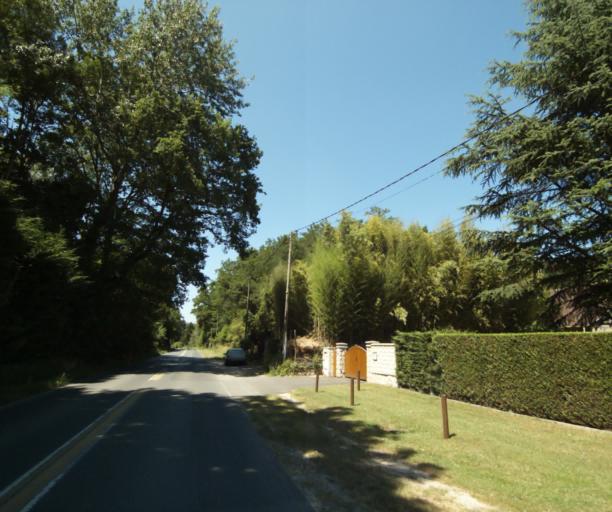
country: FR
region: Ile-de-France
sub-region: Departement de Seine-et-Marne
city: Noisy-sur-Ecole
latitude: 48.3886
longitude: 2.4927
